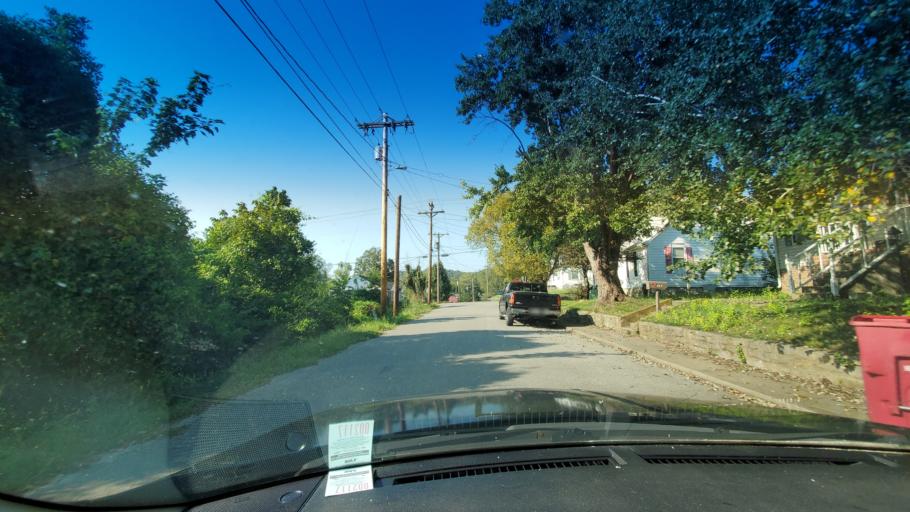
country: US
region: Tennessee
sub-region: Smith County
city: Carthage
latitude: 36.2546
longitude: -85.9528
